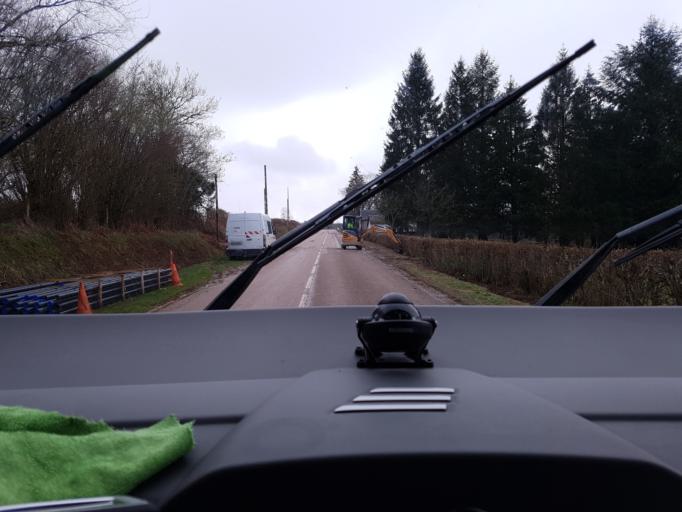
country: FR
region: Bourgogne
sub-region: Departement de la Cote-d'Or
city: Saulieu
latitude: 47.2682
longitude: 4.0288
